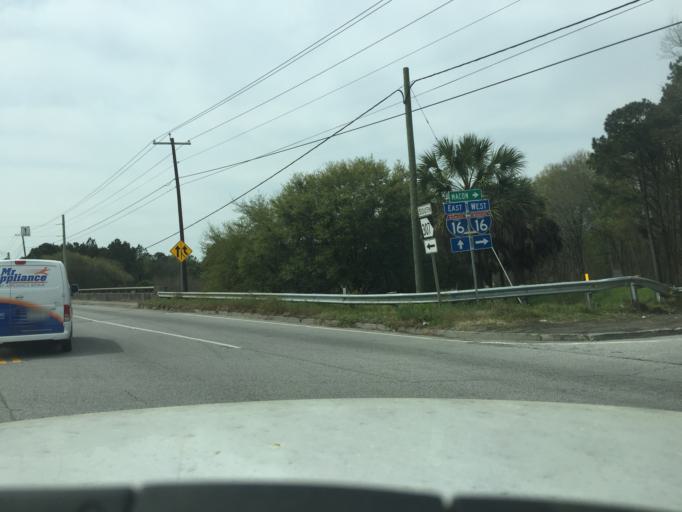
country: US
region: Georgia
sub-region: Chatham County
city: Pooler
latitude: 32.0706
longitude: -81.2022
